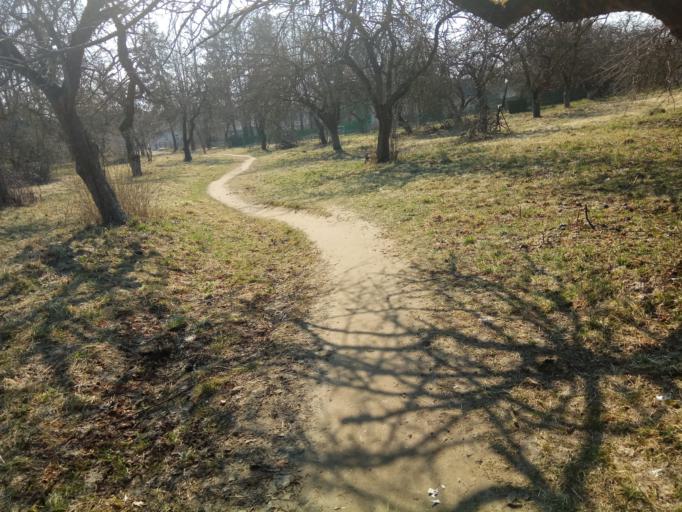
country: BY
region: Minsk
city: Valozhyn
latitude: 54.0834
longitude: 26.5174
